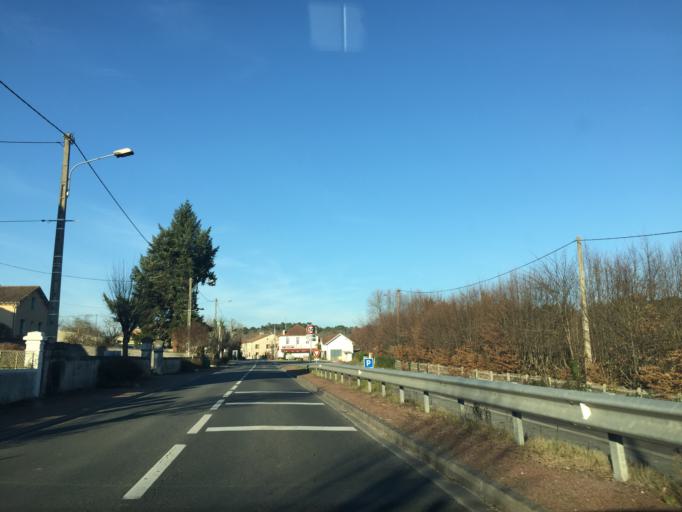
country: FR
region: Aquitaine
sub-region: Departement de la Dordogne
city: Neuvic
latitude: 45.1604
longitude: 0.3977
